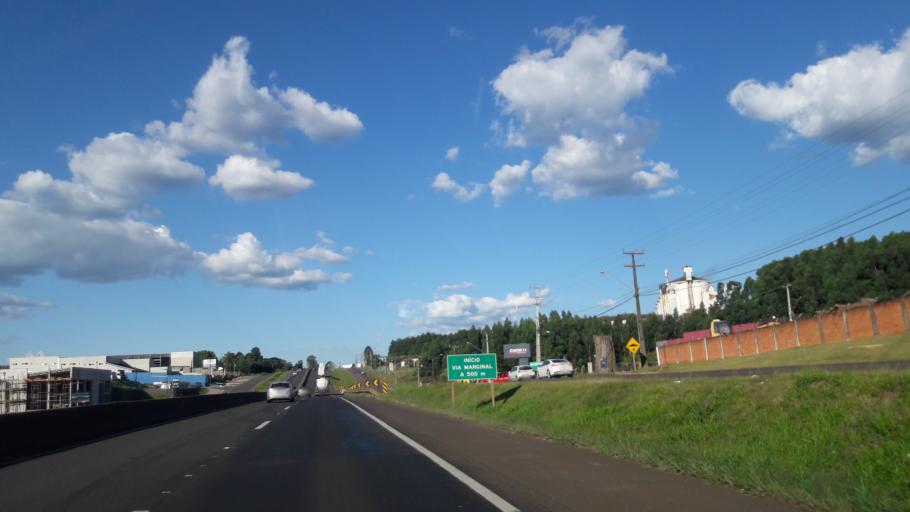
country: BR
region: Parana
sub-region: Guarapuava
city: Guarapuava
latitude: -25.3536
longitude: -51.4598
